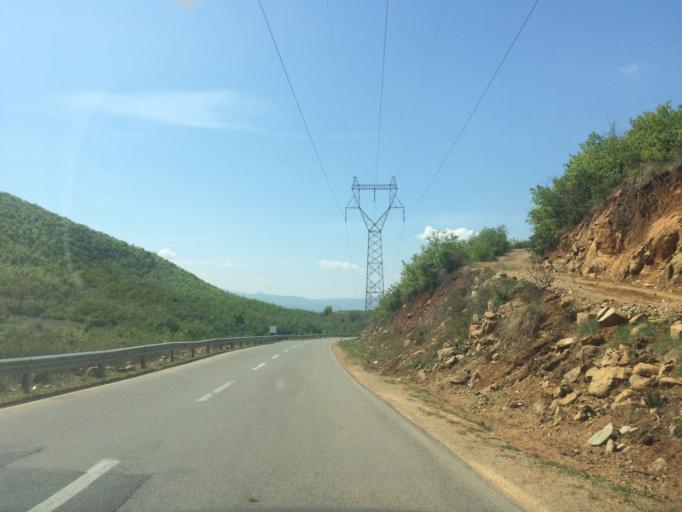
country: AL
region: Kukes
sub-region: Rrethi i Tropojes
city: Llugaj
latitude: 42.3831
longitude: 20.1344
